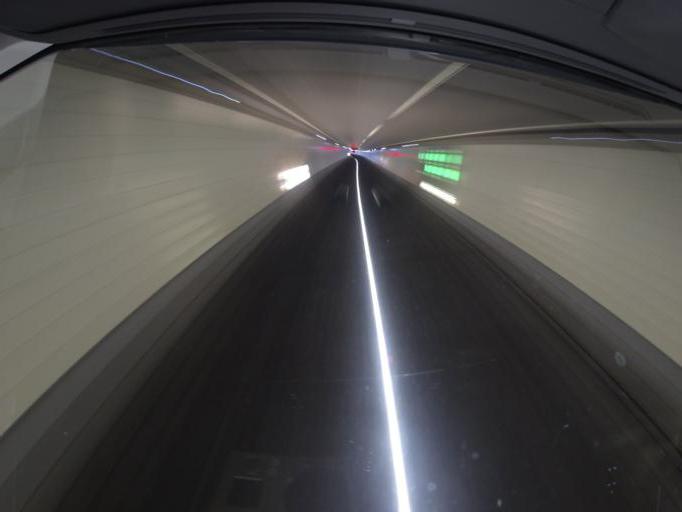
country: CH
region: Saint Gallen
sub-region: Wahlkreis Sarganserland
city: Quarten
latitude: 47.1110
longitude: 9.2173
